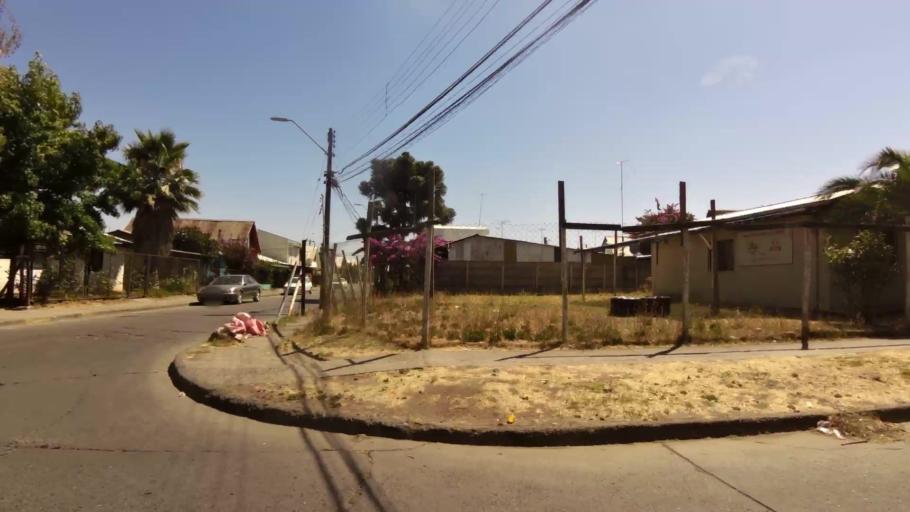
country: CL
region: Maule
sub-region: Provincia de Curico
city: Curico
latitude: -34.9713
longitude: -71.2456
